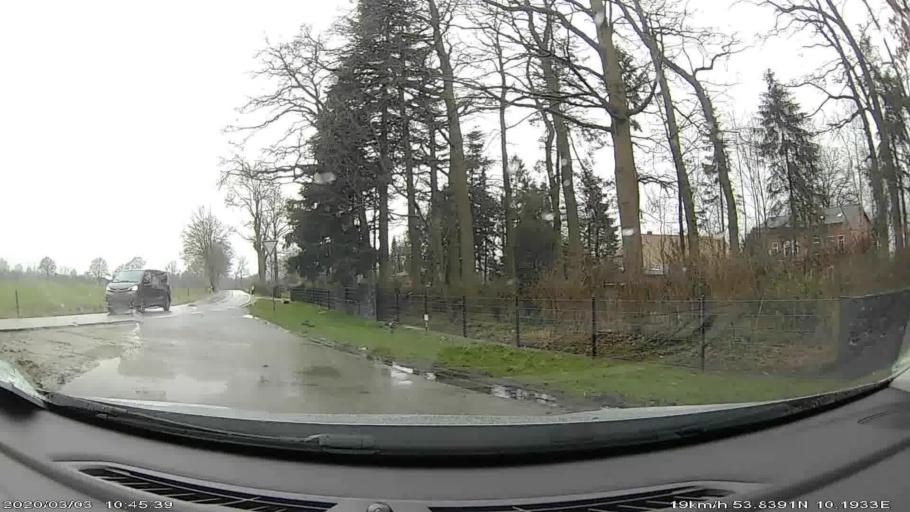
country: DE
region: Schleswig-Holstein
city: Seth
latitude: 53.8396
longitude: 10.1898
